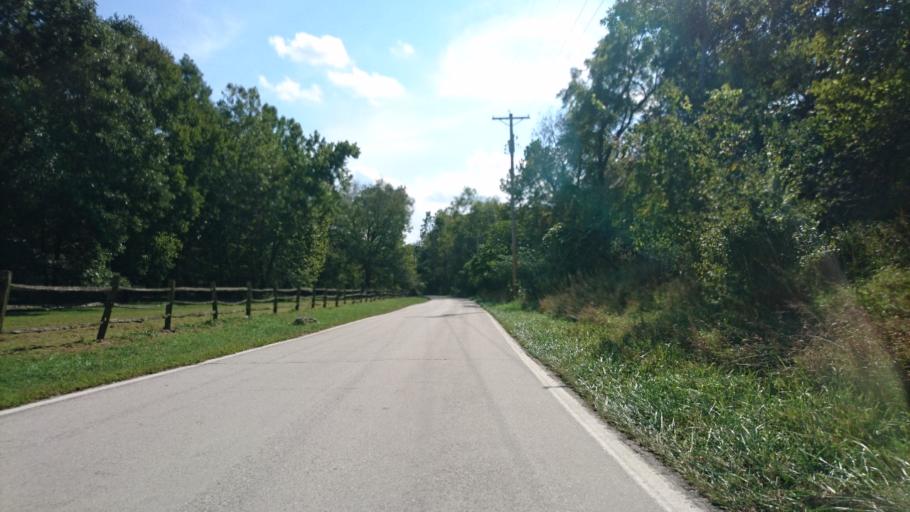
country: US
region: Missouri
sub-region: Saint Louis County
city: Wildwood
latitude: 38.5587
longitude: -90.6413
